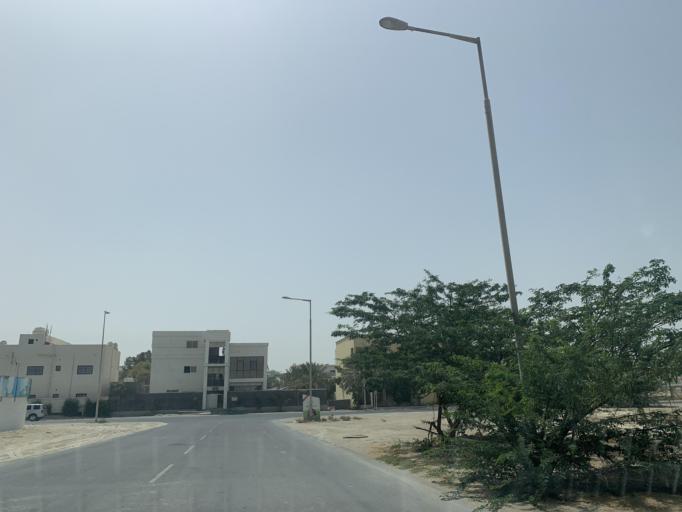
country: BH
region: Northern
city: Madinat `Isa
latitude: 26.1580
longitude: 50.5265
